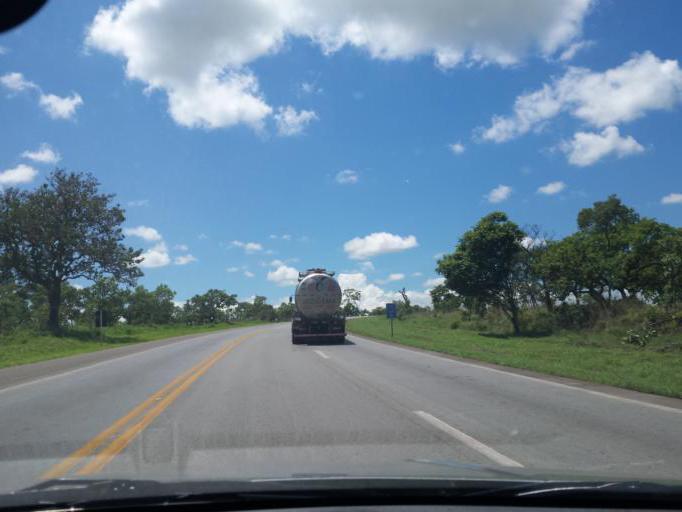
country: BR
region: Goias
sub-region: Cristalina
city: Cristalina
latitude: -16.5465
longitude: -47.7877
